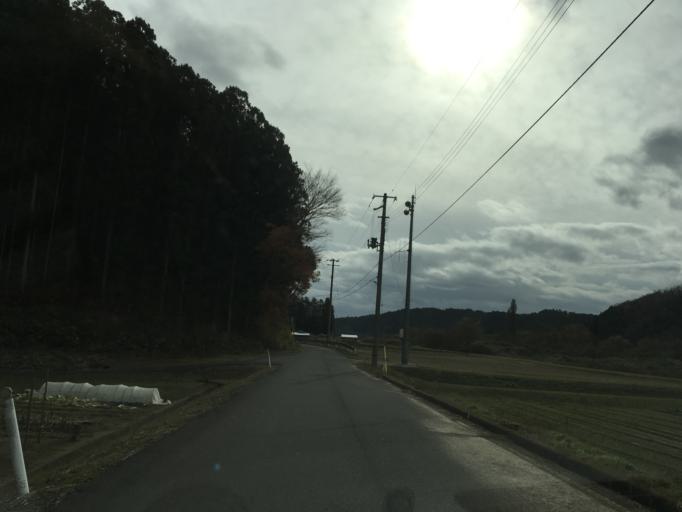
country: JP
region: Iwate
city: Ichinoseki
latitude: 38.7835
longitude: 141.2658
